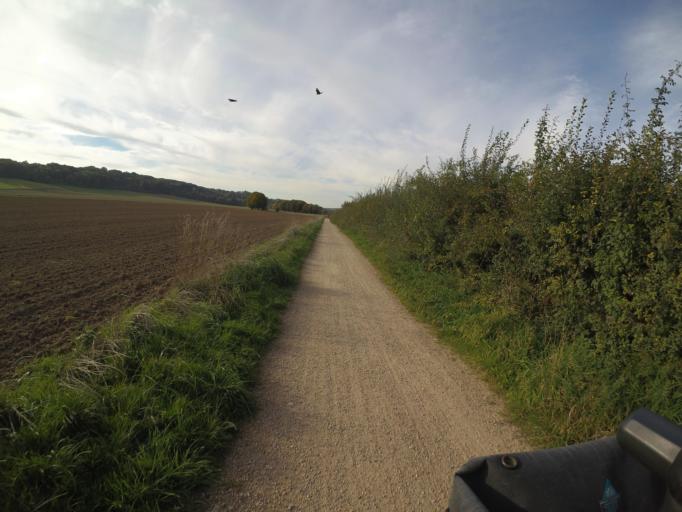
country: NL
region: Limburg
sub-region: Valkenburg aan de Geul
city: Schin op Geul
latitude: 50.8525
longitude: 5.8549
